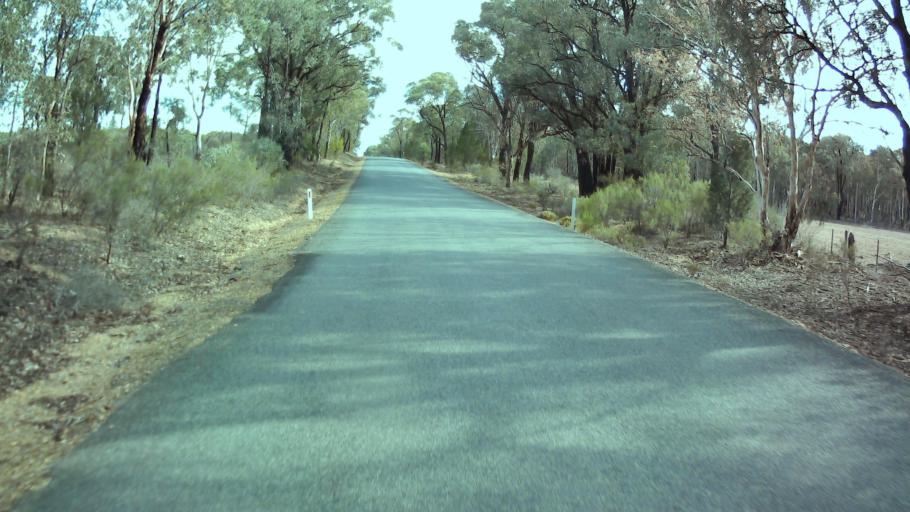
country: AU
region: New South Wales
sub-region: Weddin
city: Grenfell
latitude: -33.8803
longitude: 148.2008
